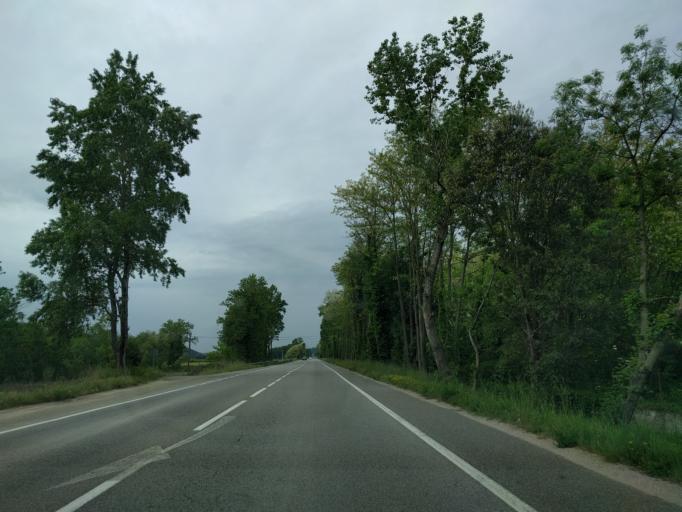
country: ES
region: Catalonia
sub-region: Provincia de Girona
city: Breda
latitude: 41.7250
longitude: 2.5701
